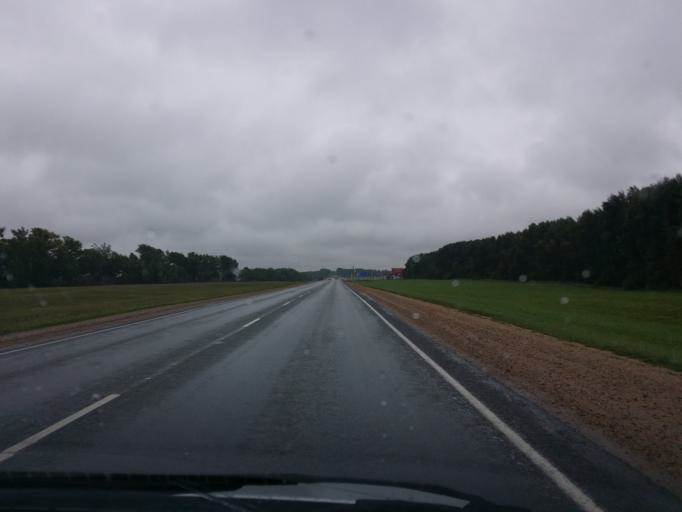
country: RU
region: Altai Krai
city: Bayunovskiye Klyuchi
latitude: 53.2915
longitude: 84.3121
